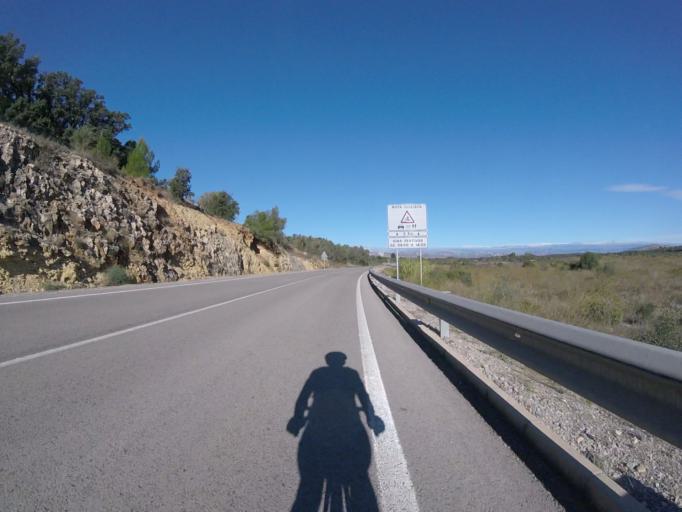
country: ES
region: Valencia
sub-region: Provincia de Castello
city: Cervera del Maestre
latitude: 40.4672
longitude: 0.2480
